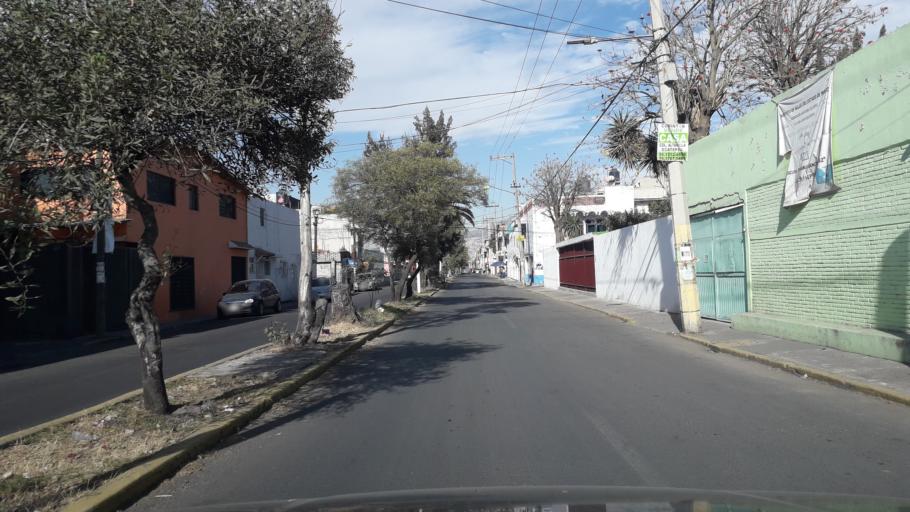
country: MX
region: Mexico City
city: Gustavo A. Madero
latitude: 19.5079
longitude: -99.0832
